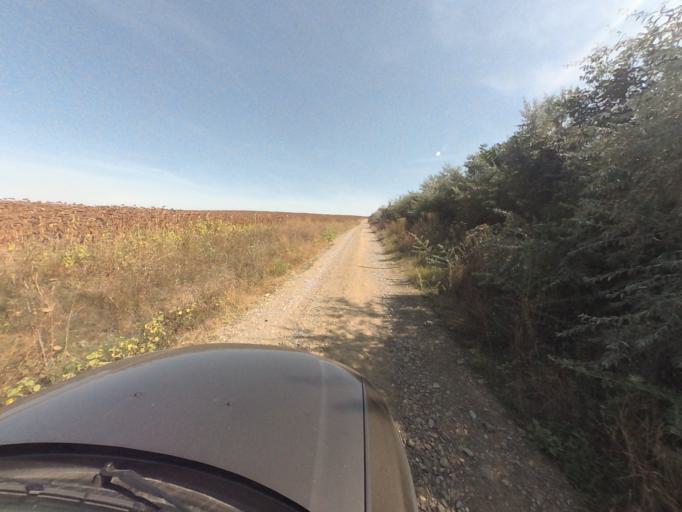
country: RO
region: Vaslui
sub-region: Comuna Deleni
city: Deleni
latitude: 46.5255
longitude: 27.7401
